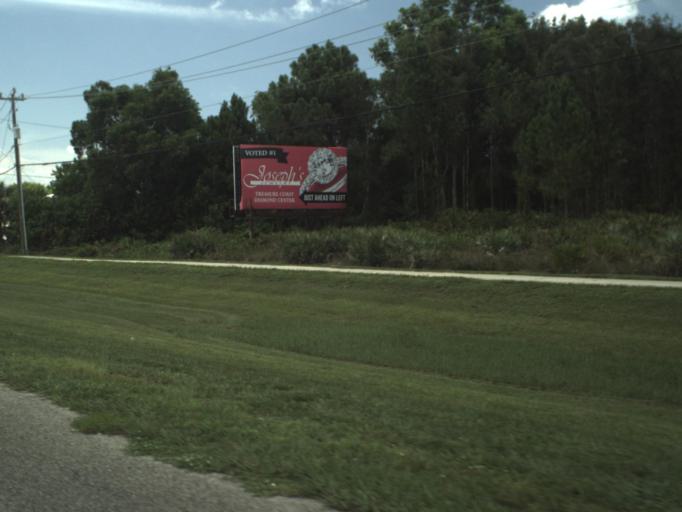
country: US
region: Florida
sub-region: Martin County
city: Port Salerno
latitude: 27.1381
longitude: -80.2095
